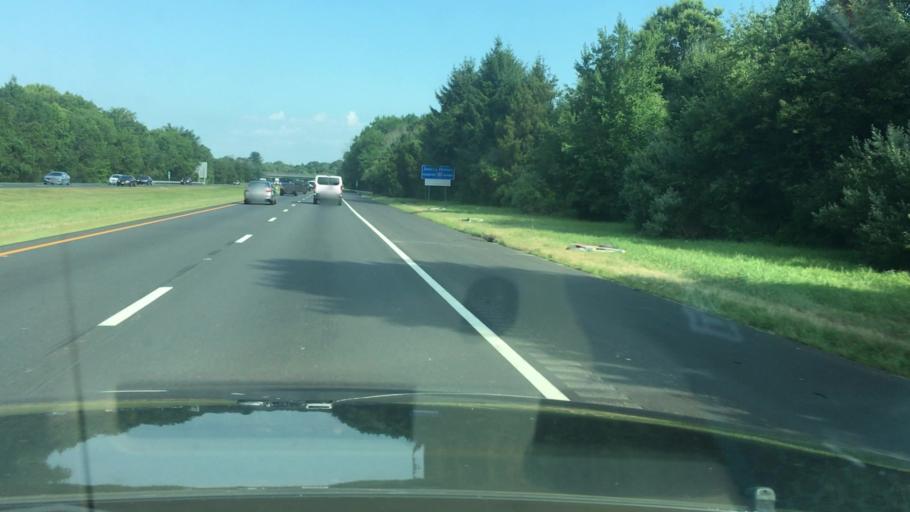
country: US
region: New Jersey
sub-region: Monmouth County
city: Shrewsbury
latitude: 40.1669
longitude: -74.4403
